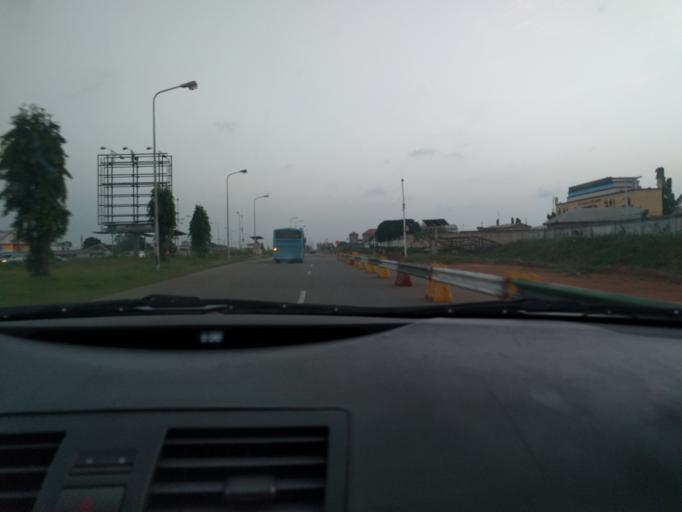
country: NG
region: Lagos
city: Oshodi
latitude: 6.5678
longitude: 3.3211
